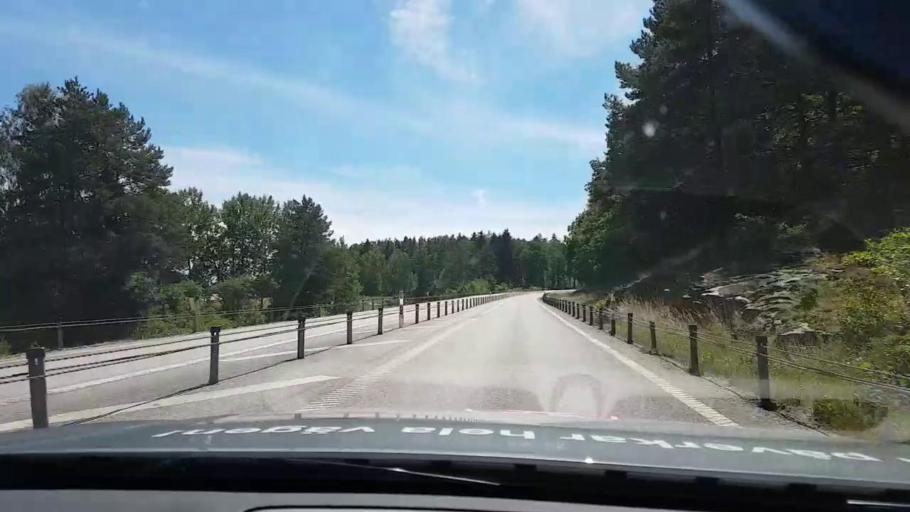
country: SE
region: Kalmar
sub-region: Vasterviks Kommun
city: Gamleby
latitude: 57.9186
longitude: 16.3996
